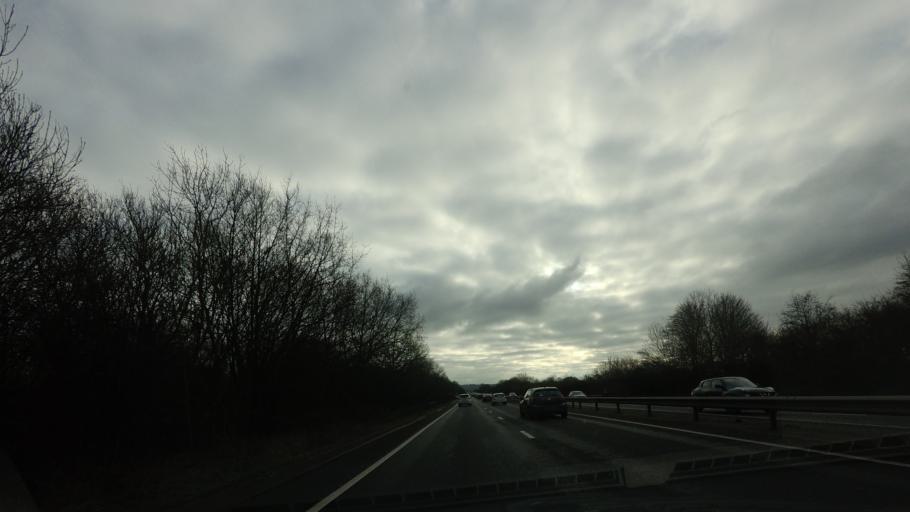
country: GB
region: England
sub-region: Kent
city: Tonbridge
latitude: 51.2051
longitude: 0.2278
